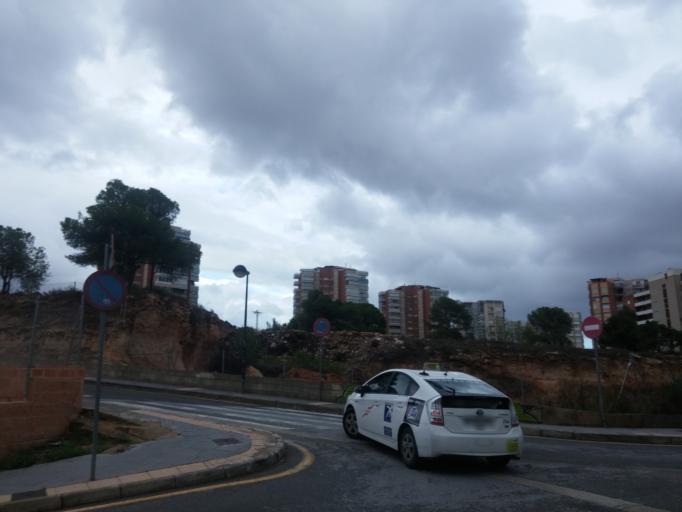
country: ES
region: Valencia
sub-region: Provincia de Alicante
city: Benidorm
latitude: 38.5388
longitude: -0.1427
